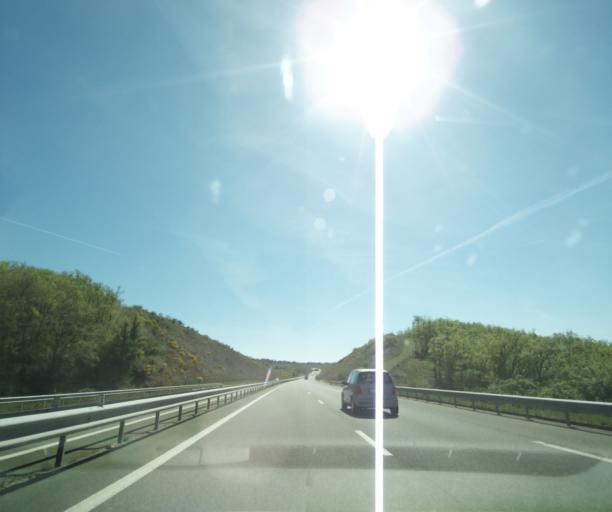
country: FR
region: Midi-Pyrenees
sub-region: Departement du Lot
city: Cahors
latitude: 44.5157
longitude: 1.5060
